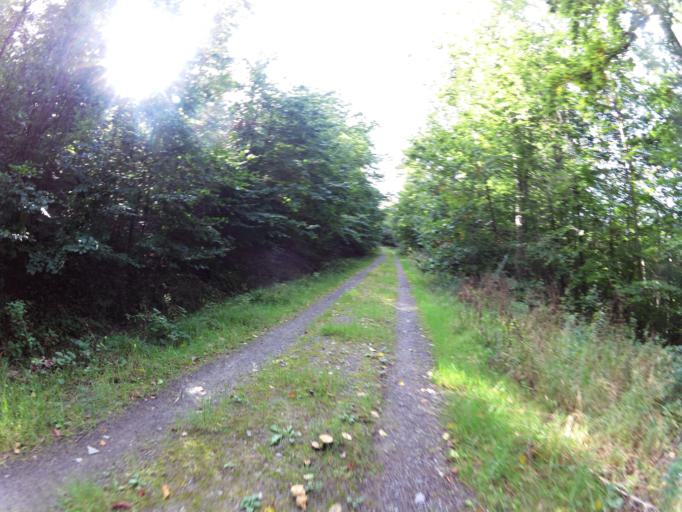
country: DE
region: Bavaria
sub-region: Regierungsbezirk Unterfranken
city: Waldbrunn
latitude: 49.7438
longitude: 9.8035
